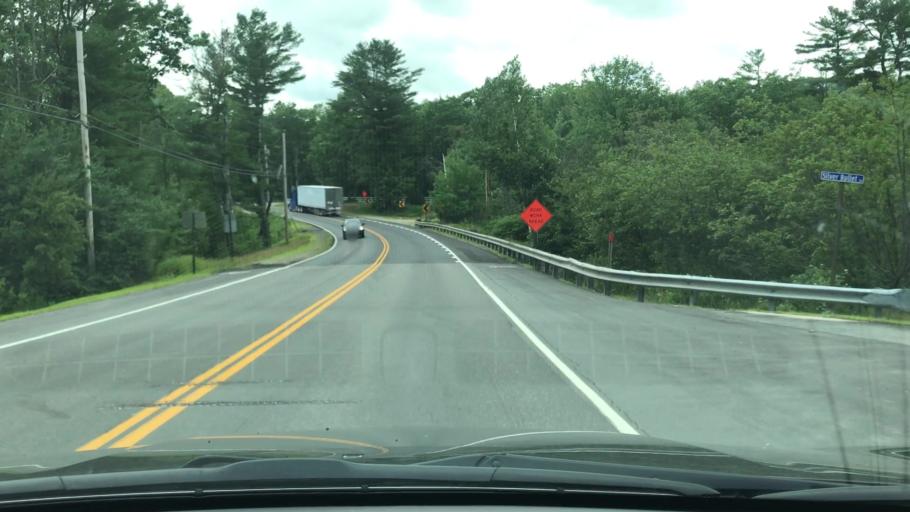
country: US
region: Maine
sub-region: Oxford County
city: West Paris
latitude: 44.3844
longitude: -70.6419
